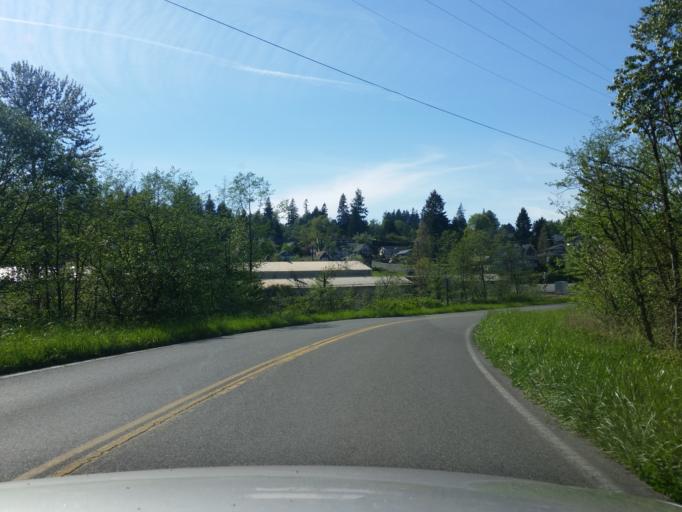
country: US
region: Washington
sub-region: Snohomish County
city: Everett
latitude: 47.9463
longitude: -122.1900
